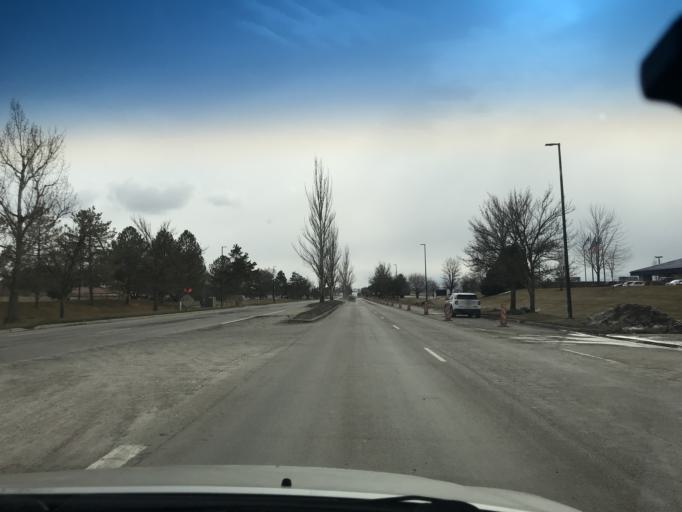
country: US
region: Utah
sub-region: Salt Lake County
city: West Valley City
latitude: 40.7796
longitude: -112.0252
